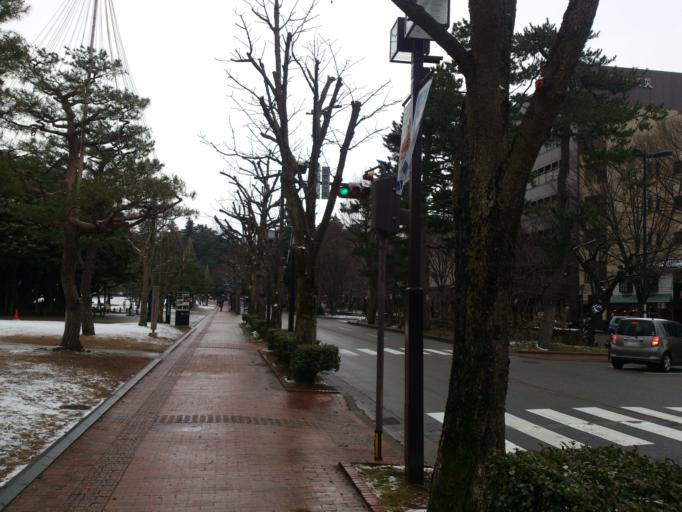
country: JP
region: Ishikawa
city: Kanazawa-shi
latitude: 36.5621
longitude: 136.6570
